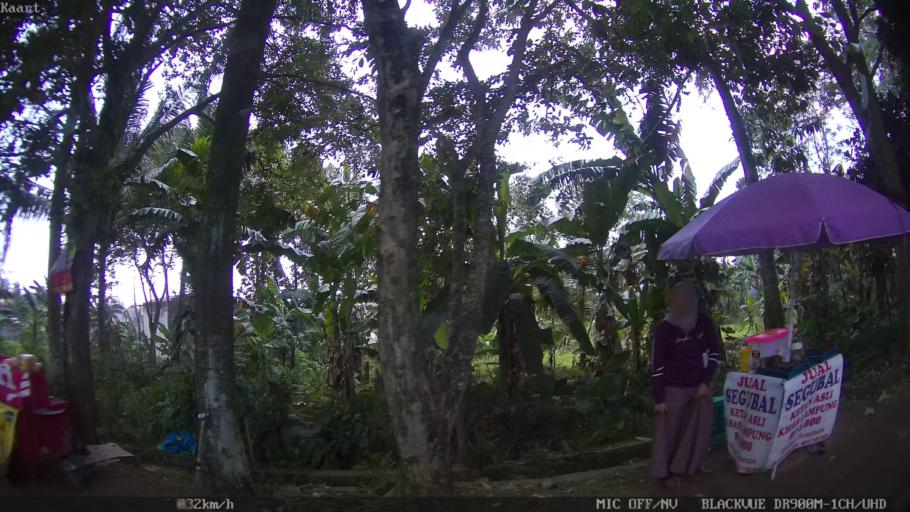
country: ID
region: Lampung
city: Kedaton
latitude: -5.3764
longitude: 105.2659
